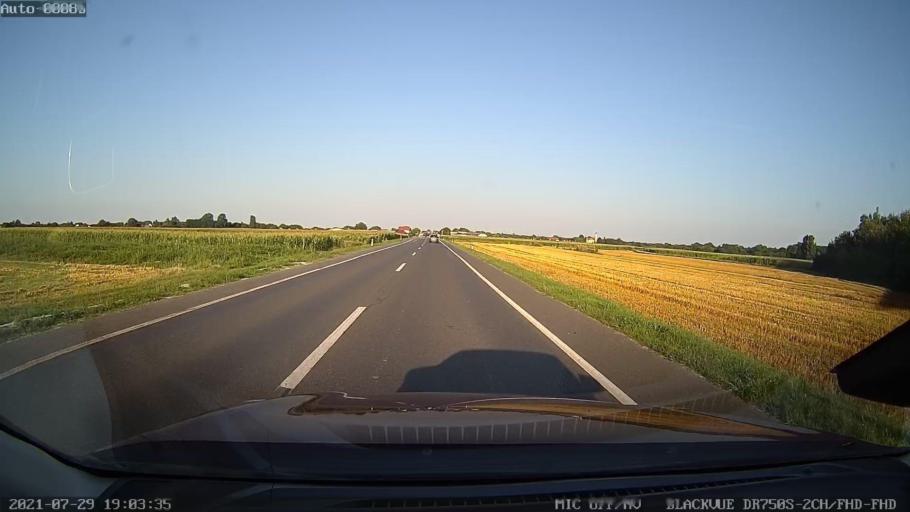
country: HR
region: Medimurska
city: Kursanec
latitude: 46.2976
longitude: 16.4245
